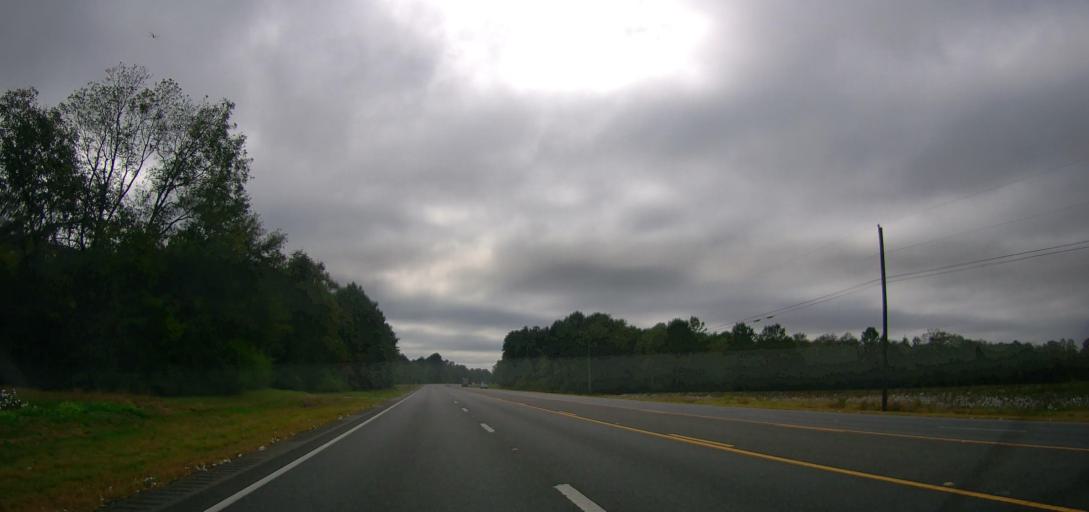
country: US
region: Georgia
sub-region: Colquitt County
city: Moultrie
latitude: 31.0653
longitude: -83.8270
